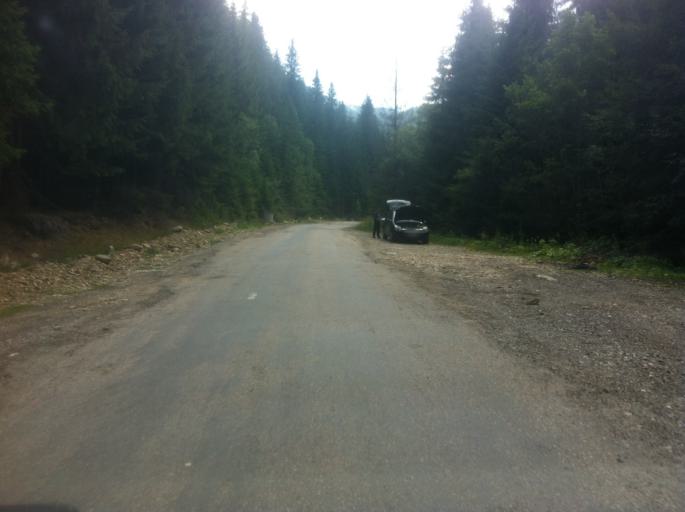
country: RO
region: Hunedoara
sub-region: Oras Petrila
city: Petrila
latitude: 45.4066
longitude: 23.5618
